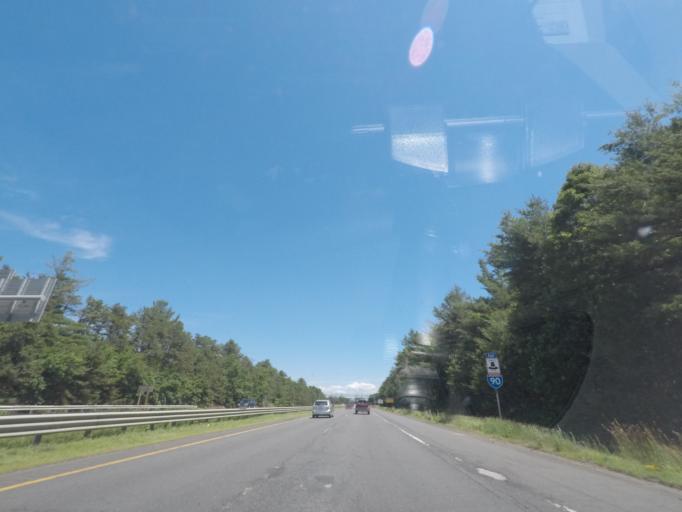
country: US
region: Massachusetts
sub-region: Hampden County
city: Westfield
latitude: 42.1441
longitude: -72.7307
